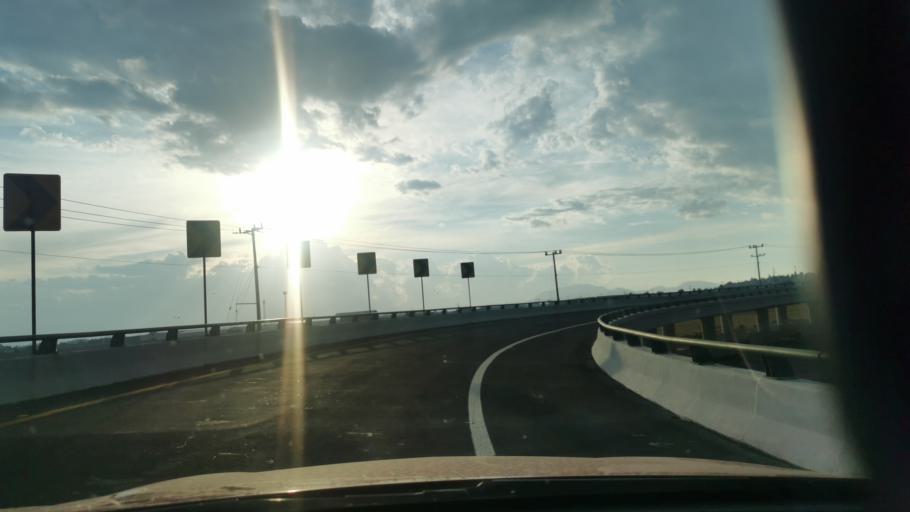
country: MX
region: Mexico
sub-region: Lerma
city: Colonia Isidro Fabela
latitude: 19.3202
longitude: -99.5224
